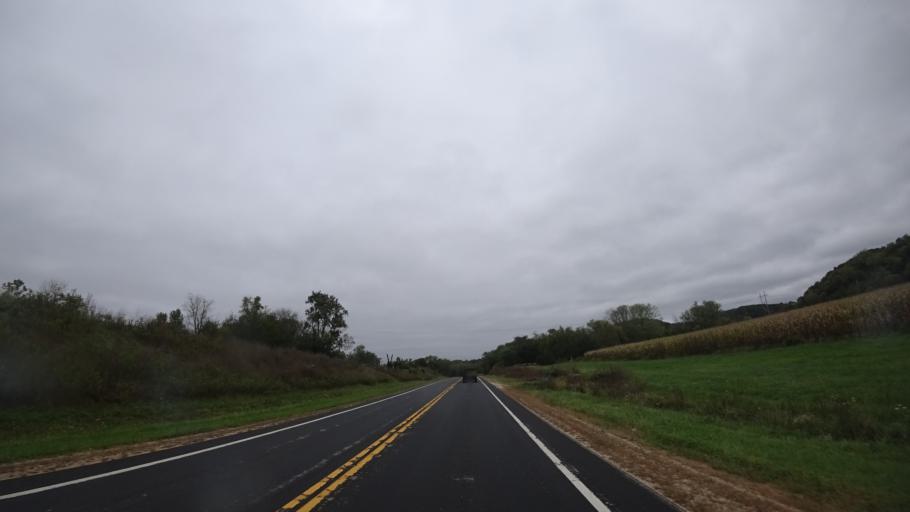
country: US
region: Wisconsin
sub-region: Grant County
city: Boscobel
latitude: 43.1123
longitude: -90.7974
